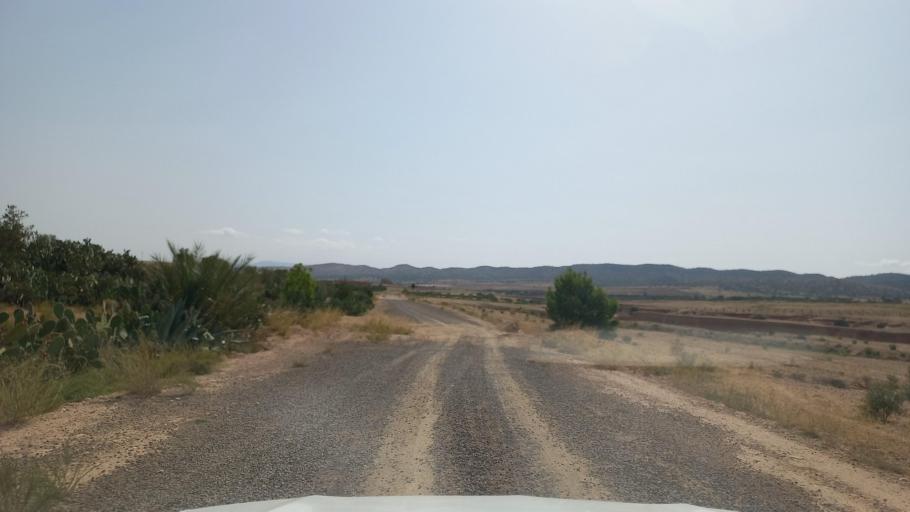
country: TN
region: Al Qasrayn
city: Sbiba
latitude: 35.3939
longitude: 8.9533
